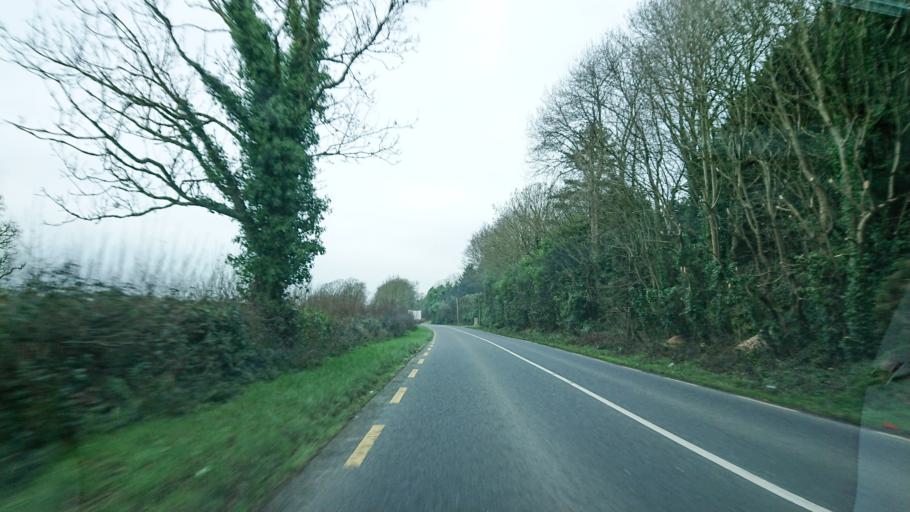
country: IE
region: Munster
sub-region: County Cork
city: Bandon
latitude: 51.7465
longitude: -8.7739
